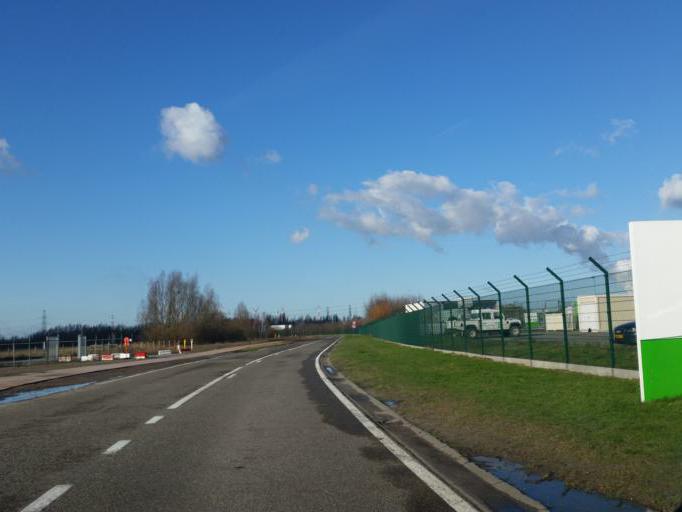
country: BE
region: Flanders
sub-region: Provincie Antwerpen
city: Zwijndrecht
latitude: 51.2479
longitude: 4.3065
